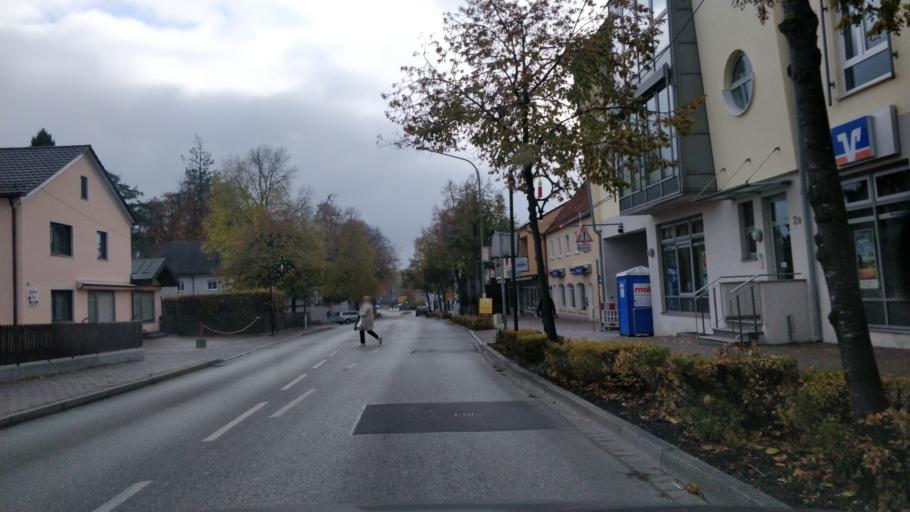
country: DE
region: Bavaria
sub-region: Swabia
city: Friedberg
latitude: 48.3547
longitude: 10.9845
